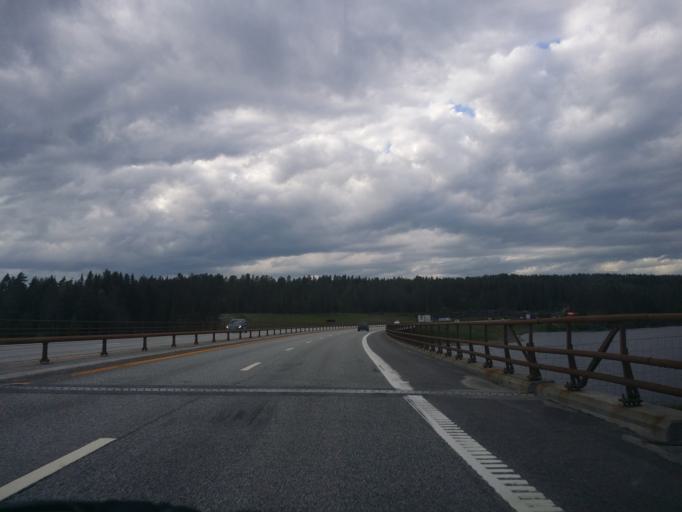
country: NO
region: Akershus
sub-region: Eidsvoll
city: Raholt
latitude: 60.2851
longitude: 11.1366
